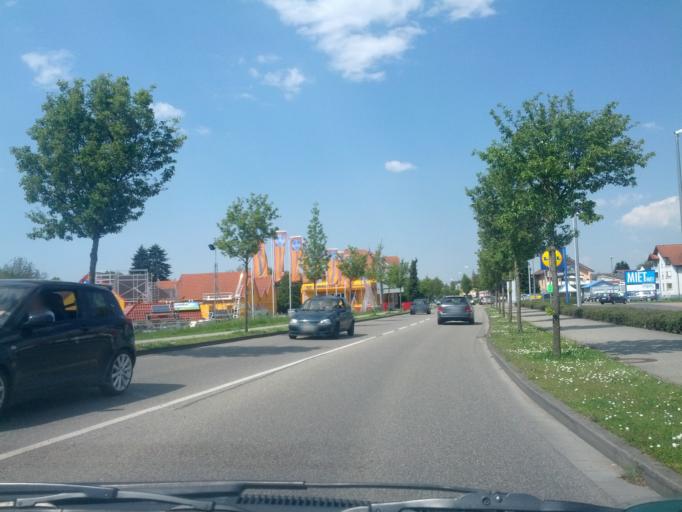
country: DE
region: Baden-Wuerttemberg
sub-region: Freiburg Region
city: Kenzingen
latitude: 48.1858
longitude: 7.7654
